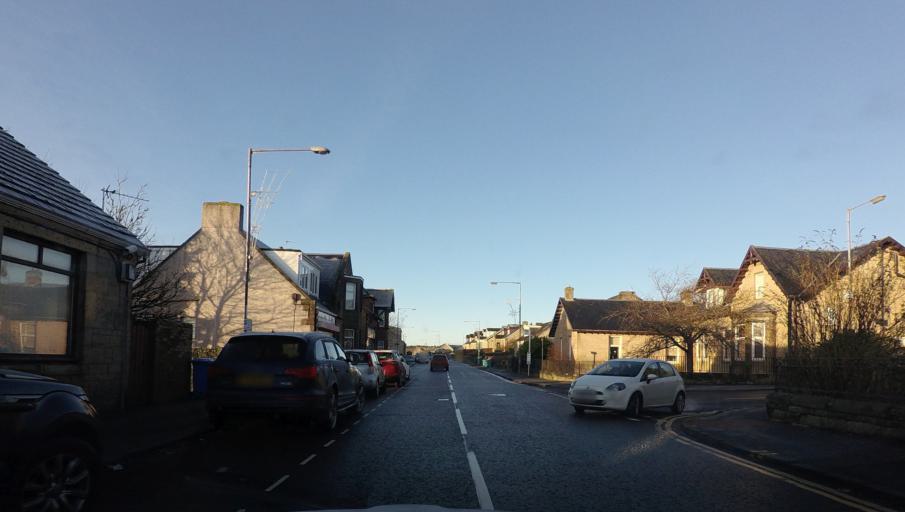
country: GB
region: Scotland
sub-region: North Lanarkshire
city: Shotts
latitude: 55.8191
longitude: -3.7994
